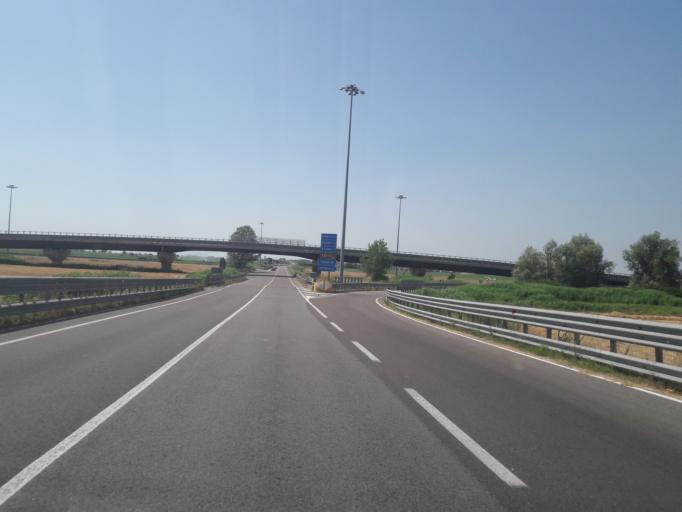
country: IT
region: Veneto
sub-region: Provincia di Rovigo
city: Bottrighe
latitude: 45.0416
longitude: 12.1004
